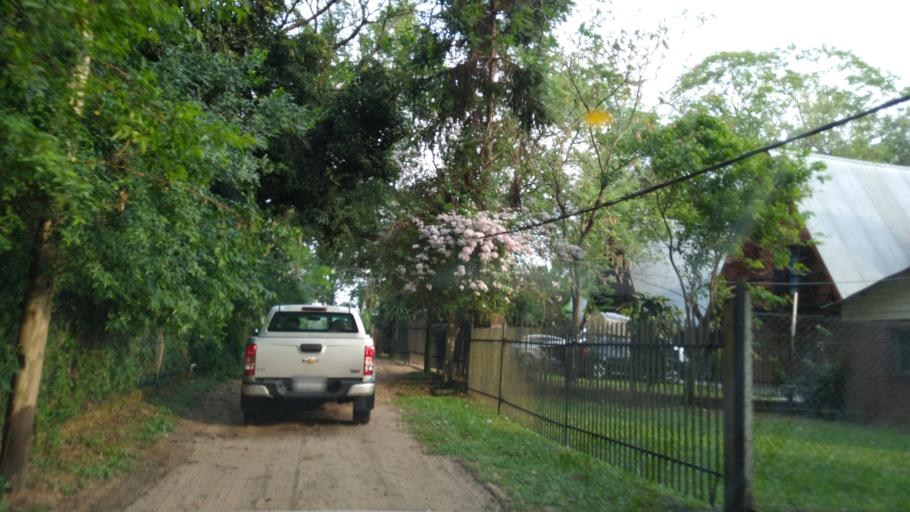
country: AR
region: Corrientes
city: Ituzaingo
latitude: -27.5928
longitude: -56.7078
